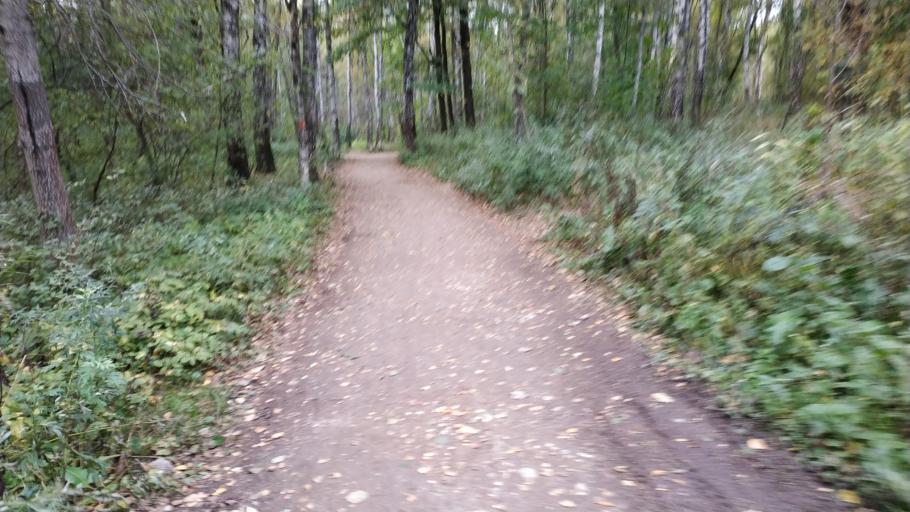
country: RU
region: Moscow
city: Khimki
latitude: 55.8685
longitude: 37.4312
